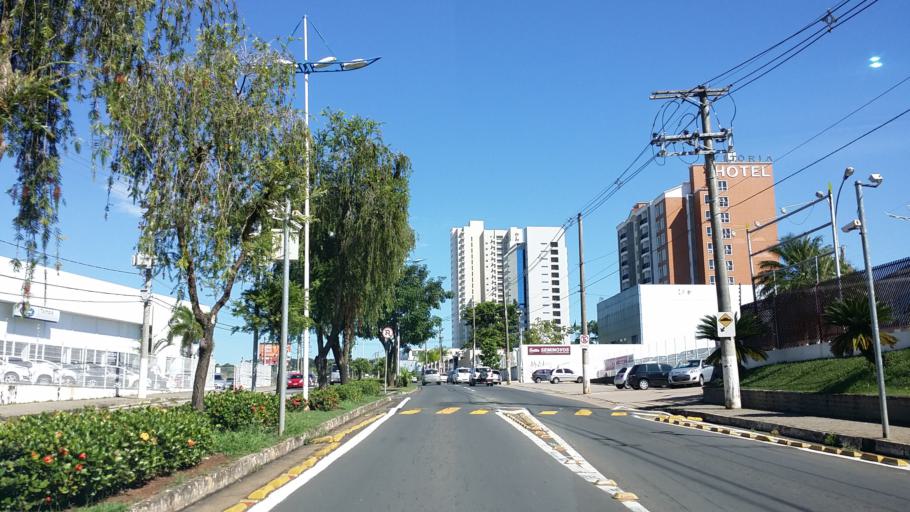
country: BR
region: Sao Paulo
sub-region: Indaiatuba
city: Indaiatuba
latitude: -23.0865
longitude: -47.1808
